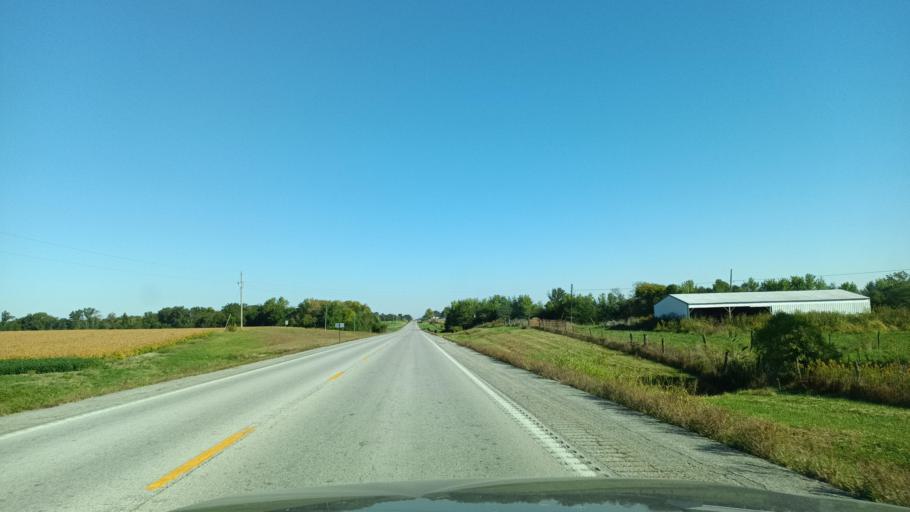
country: US
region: Missouri
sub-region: Audrain County
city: Vandalia
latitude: 39.2997
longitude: -91.6438
